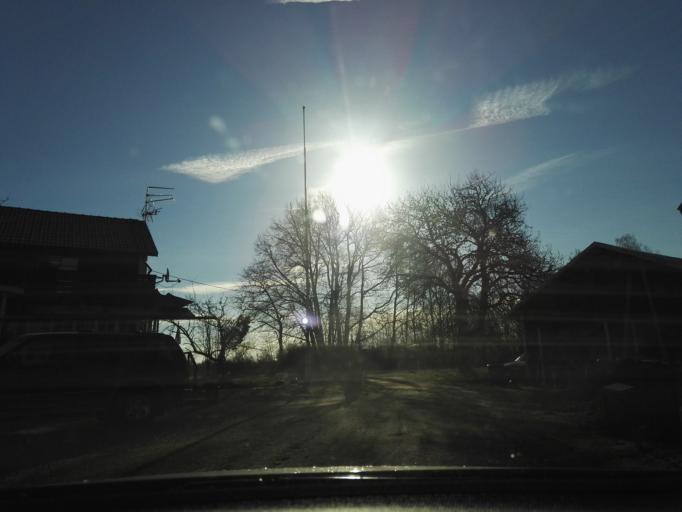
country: SE
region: Kronoberg
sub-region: Vaxjo Kommun
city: Vaexjoe
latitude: 56.9569
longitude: 14.7593
